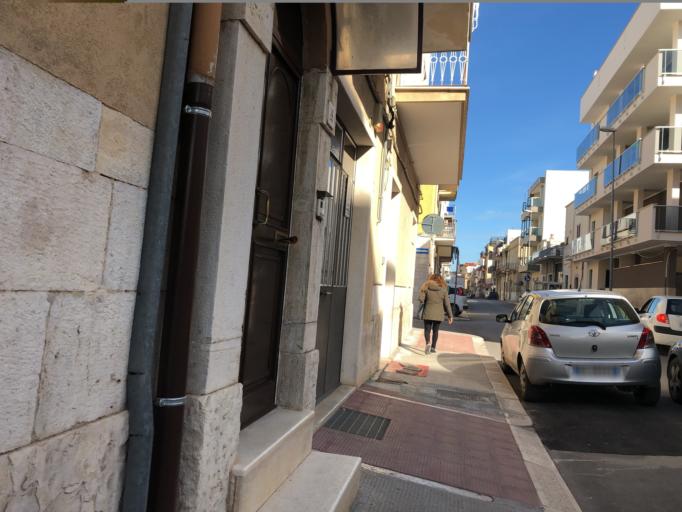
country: IT
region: Apulia
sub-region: Provincia di Barletta - Andria - Trani
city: Andria
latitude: 41.2211
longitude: 16.3040
